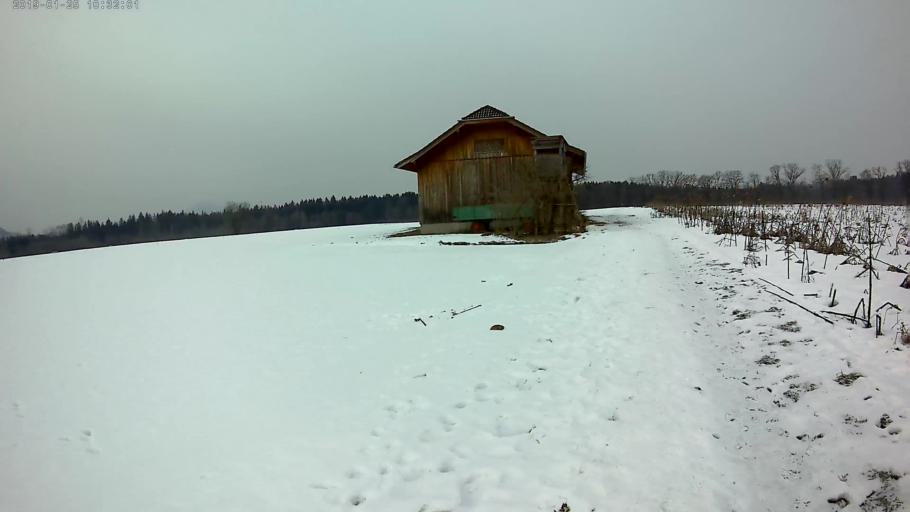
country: AT
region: Salzburg
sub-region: Politischer Bezirk Salzburg-Umgebung
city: Anif
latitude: 47.7578
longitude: 13.0554
